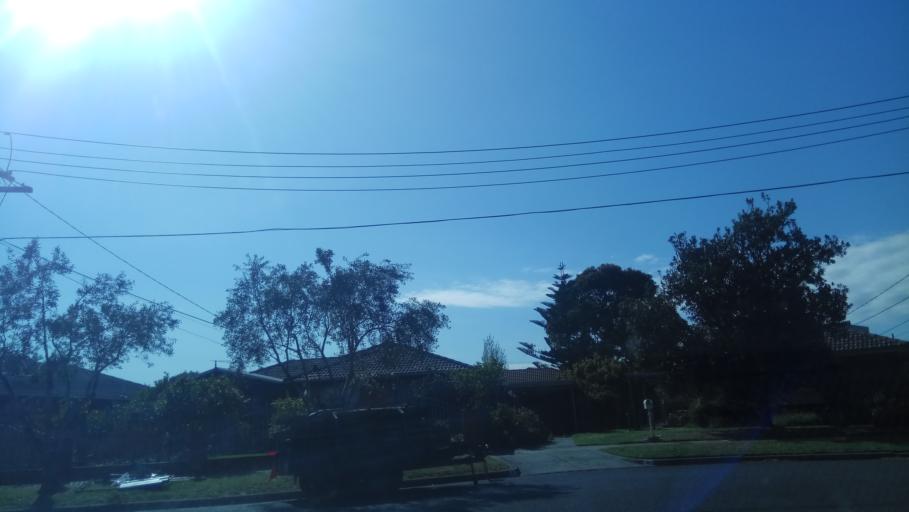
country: AU
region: Victoria
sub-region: Kingston
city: Clayton South
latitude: -37.9455
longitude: 145.1143
